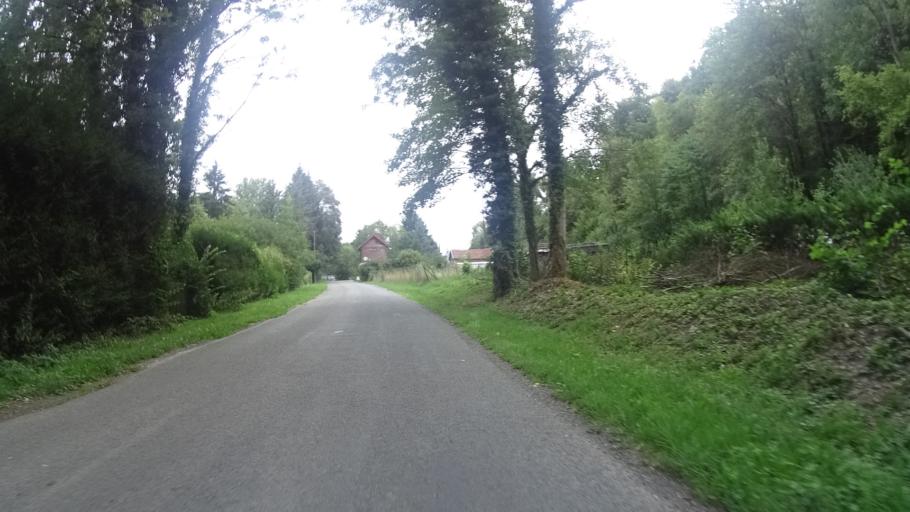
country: FR
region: Picardie
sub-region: Departement de l'Aisne
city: Guise
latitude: 49.8968
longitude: 3.5604
